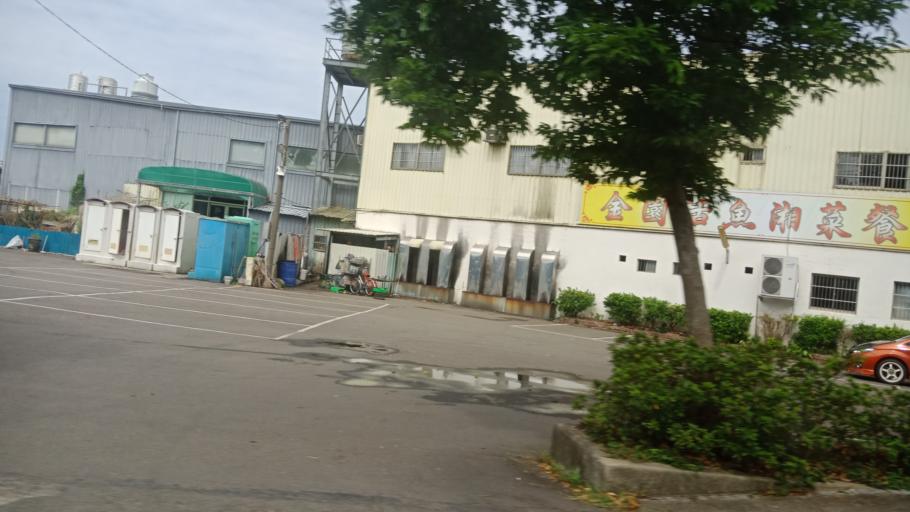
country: TW
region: Taiwan
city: Daxi
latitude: 24.8426
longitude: 121.2409
